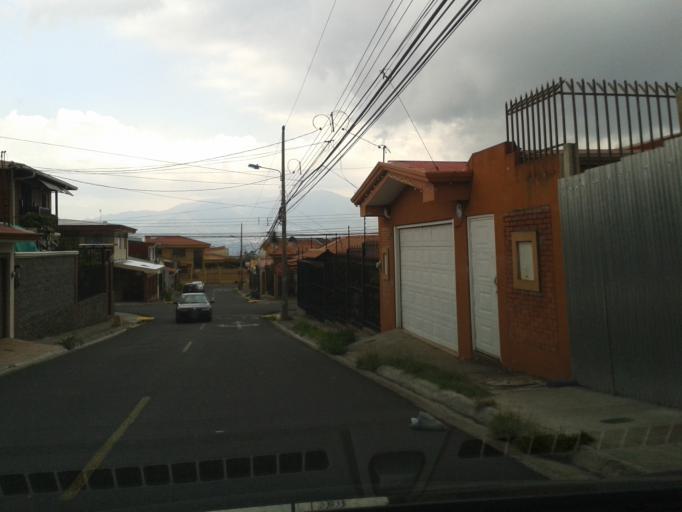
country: CR
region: Heredia
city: San Francisco
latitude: 9.9939
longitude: -84.1276
